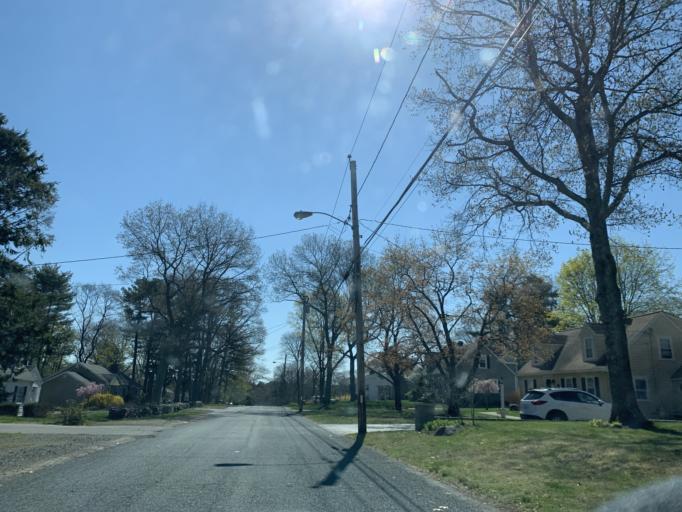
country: US
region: Massachusetts
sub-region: Norfolk County
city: Walpole
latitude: 42.1503
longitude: -71.2172
